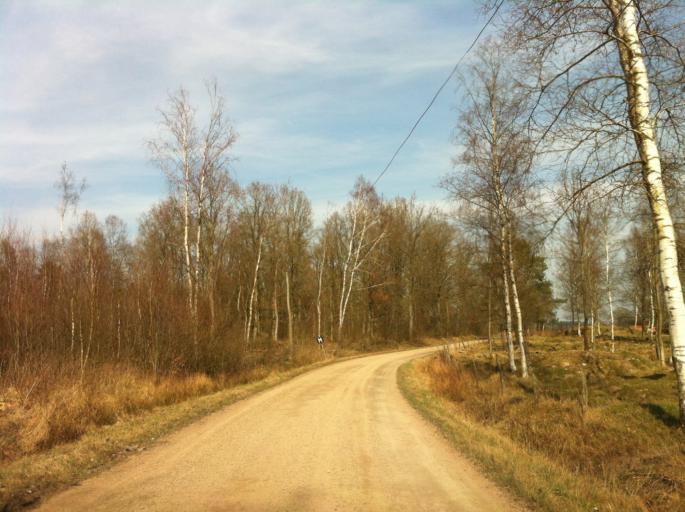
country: SE
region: Skane
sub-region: Eslovs Kommun
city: Stehag
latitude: 56.0133
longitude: 13.3538
